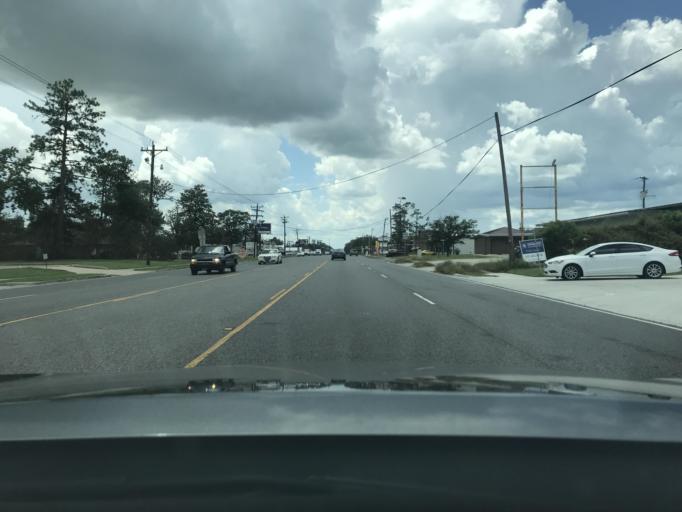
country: US
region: Louisiana
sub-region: Calcasieu Parish
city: Moss Bluff
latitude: 30.3007
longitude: -93.2087
